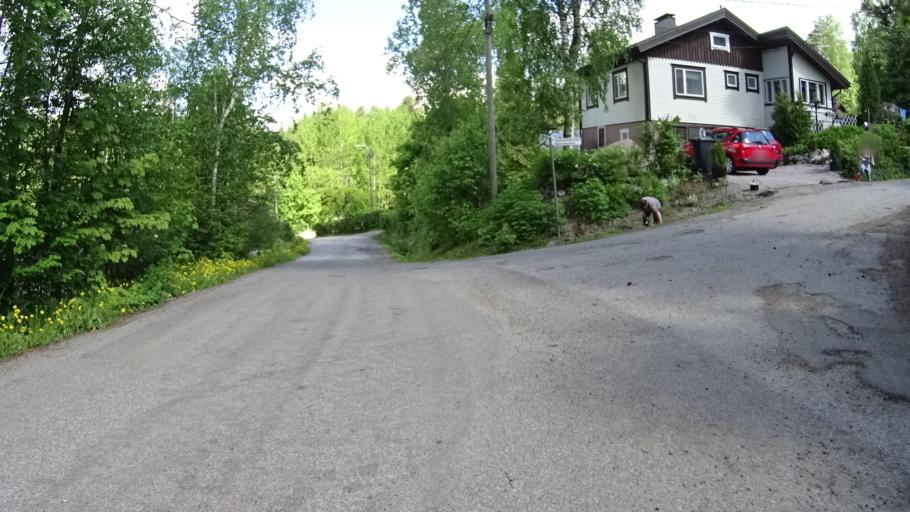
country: FI
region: Uusimaa
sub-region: Helsinki
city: Espoo
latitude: 60.2245
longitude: 24.6308
